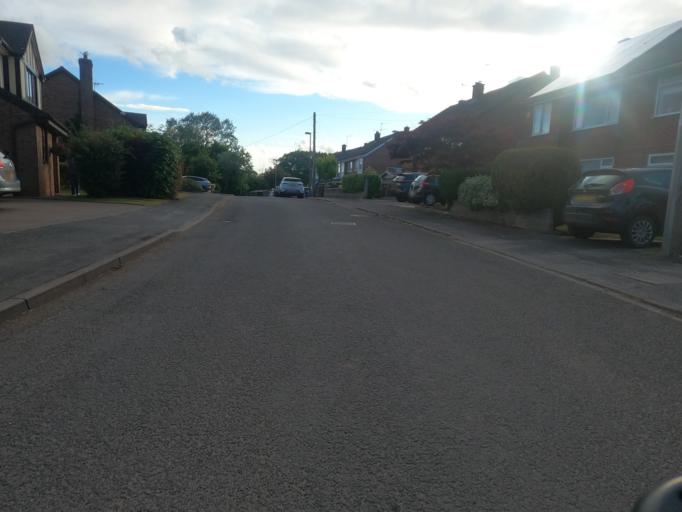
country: GB
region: England
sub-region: Cheshire West and Chester
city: Northwich
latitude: 53.2339
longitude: -2.5225
